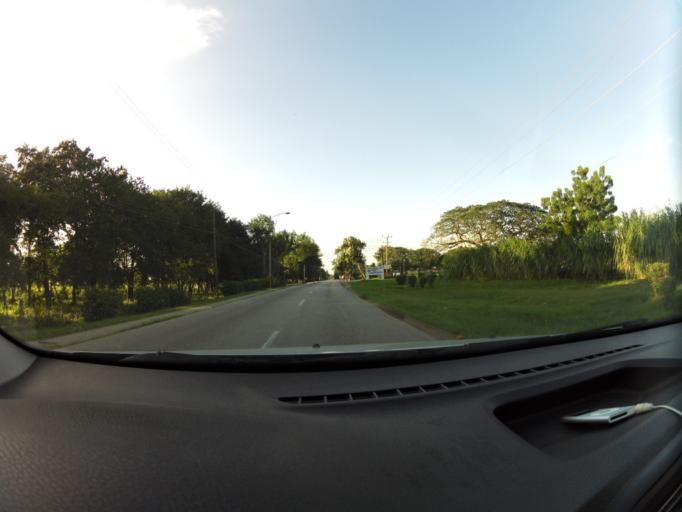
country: CU
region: Granma
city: Bayamo
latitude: 20.3679
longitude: -76.6597
